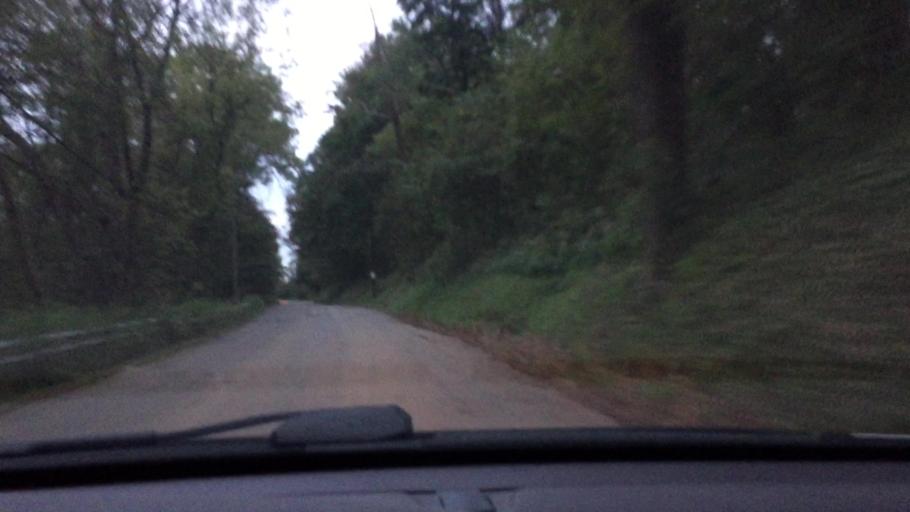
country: US
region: Pennsylvania
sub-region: Westmoreland County
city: West Newton
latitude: 40.2135
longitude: -79.7822
